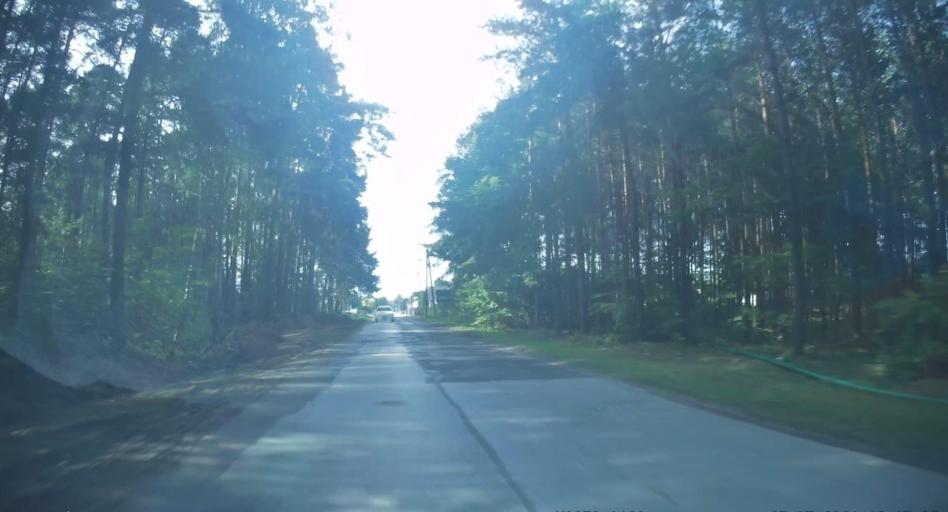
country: PL
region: Swietokrzyskie
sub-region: Powiat konecki
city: Konskie
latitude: 51.2374
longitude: 20.3811
